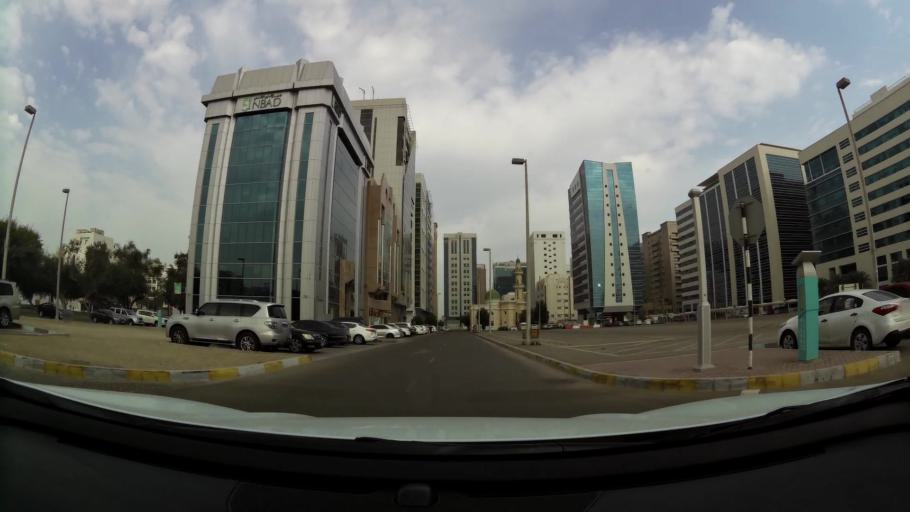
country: AE
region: Abu Dhabi
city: Abu Dhabi
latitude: 24.4623
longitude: 54.3875
